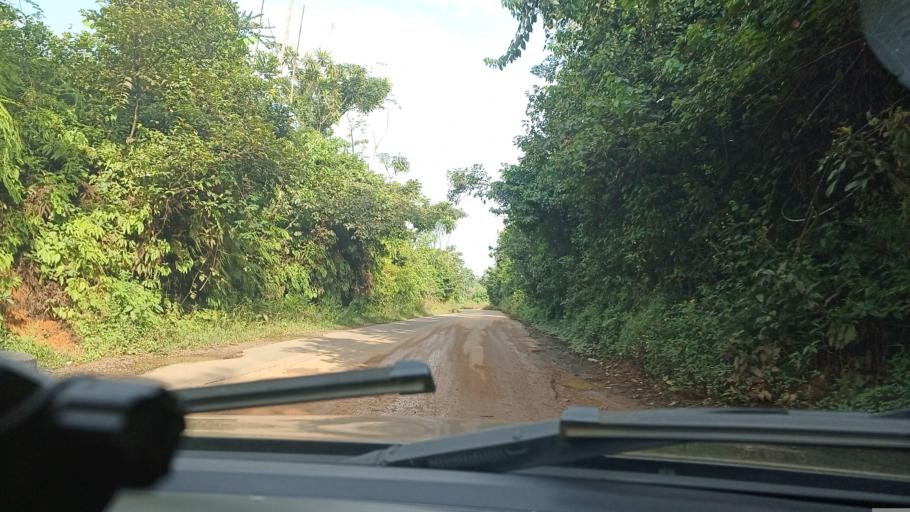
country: LR
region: Bomi
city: Tubmanburg
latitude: 6.7039
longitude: -10.9221
